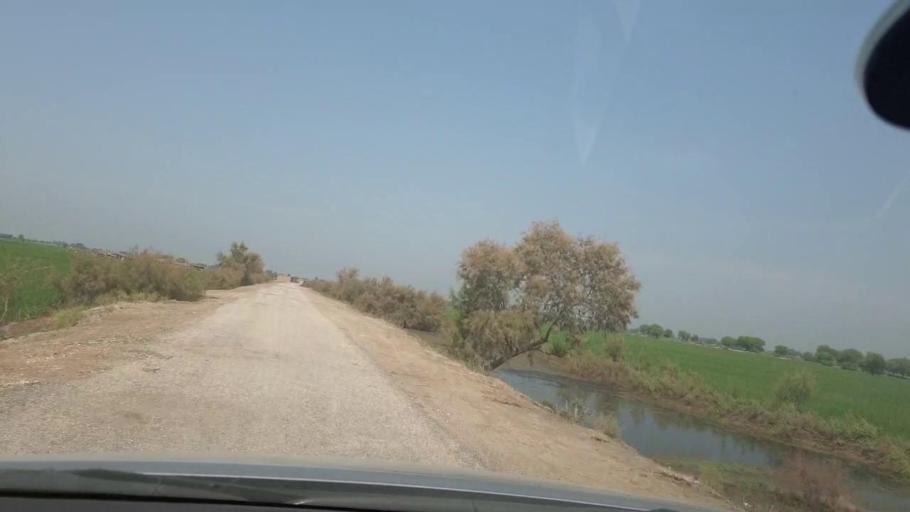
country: PK
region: Balochistan
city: Mehrabpur
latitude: 28.0694
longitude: 68.0538
